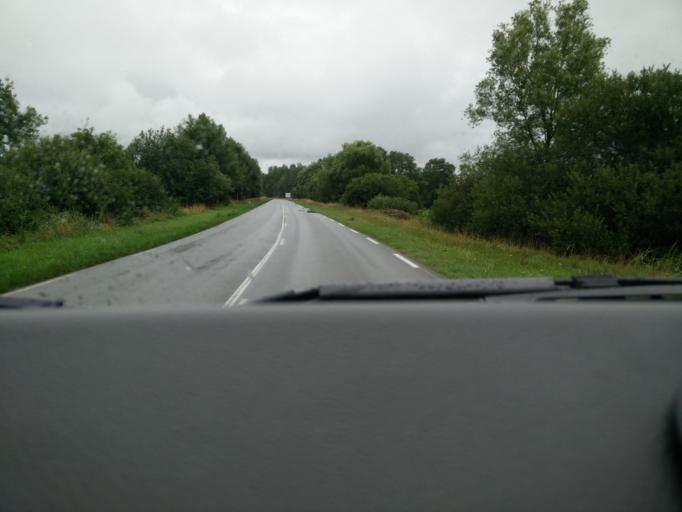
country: FR
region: Picardie
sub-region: Departement de la Somme
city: Rue
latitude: 50.2560
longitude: 1.6649
